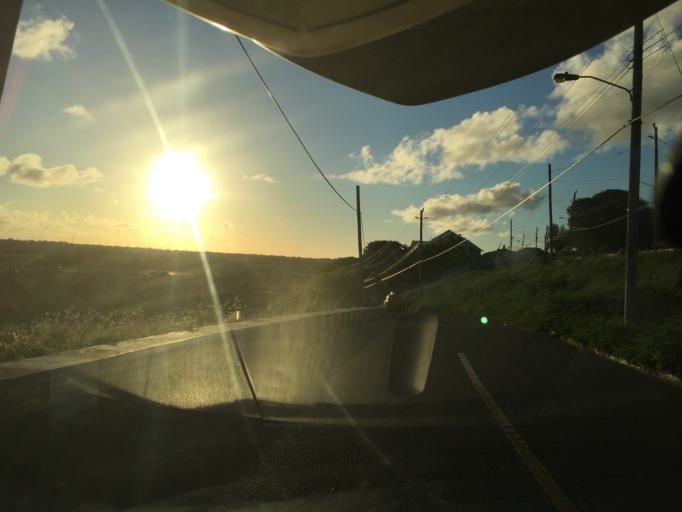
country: BB
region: Christ Church
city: Oistins
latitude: 13.0668
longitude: -59.5083
